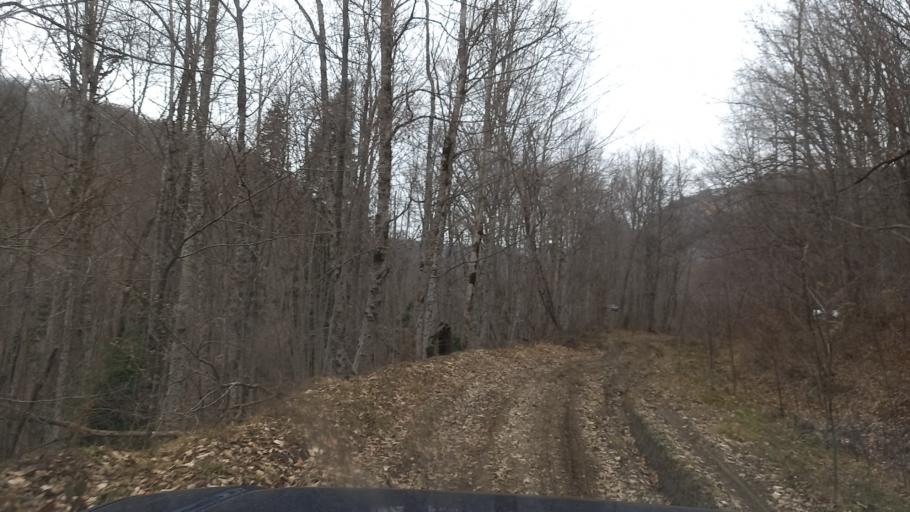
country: RU
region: Adygeya
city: Kamennomostskiy
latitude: 44.1109
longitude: 40.1044
